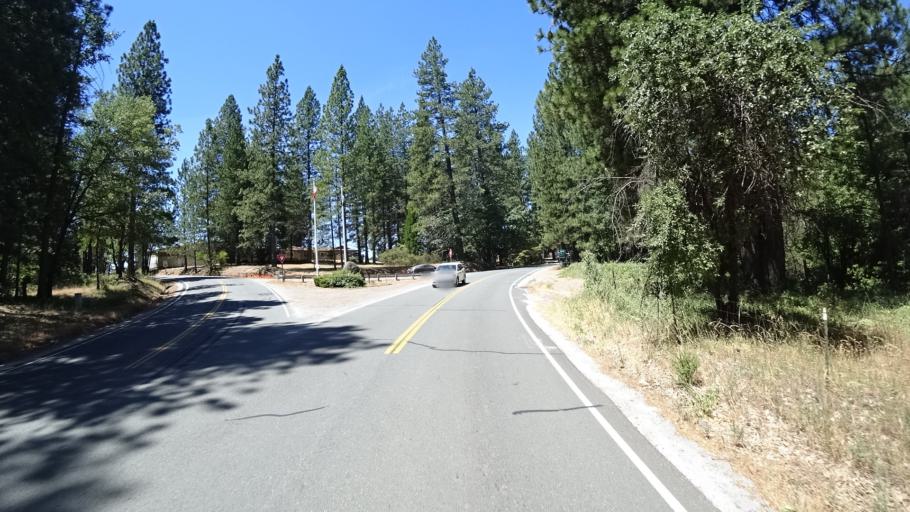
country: US
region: California
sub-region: Amador County
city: Pioneer
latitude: 38.4028
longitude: -120.5245
